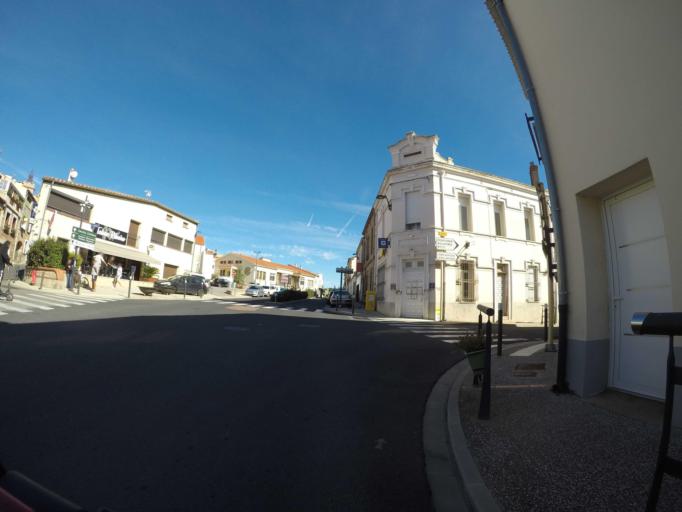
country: FR
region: Languedoc-Roussillon
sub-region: Departement des Pyrenees-Orientales
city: Ponteilla
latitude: 42.6256
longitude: 2.8139
